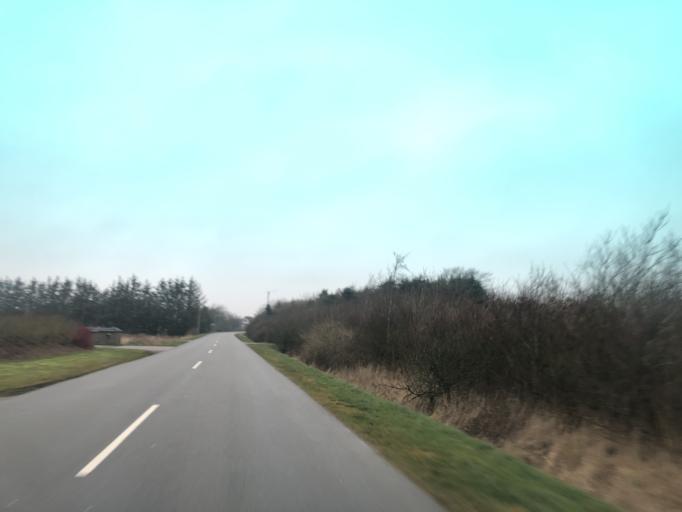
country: DK
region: North Denmark
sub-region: Thisted Kommune
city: Hurup
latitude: 56.7421
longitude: 8.4185
